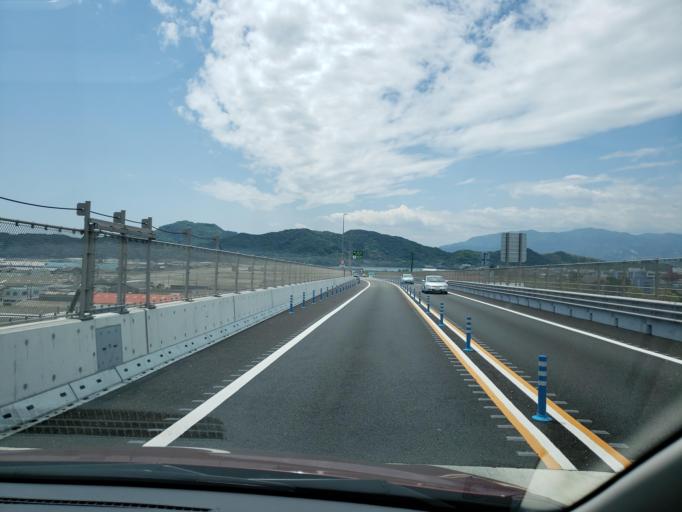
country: JP
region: Tokushima
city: Tokushima-shi
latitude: 34.0500
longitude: 134.5860
